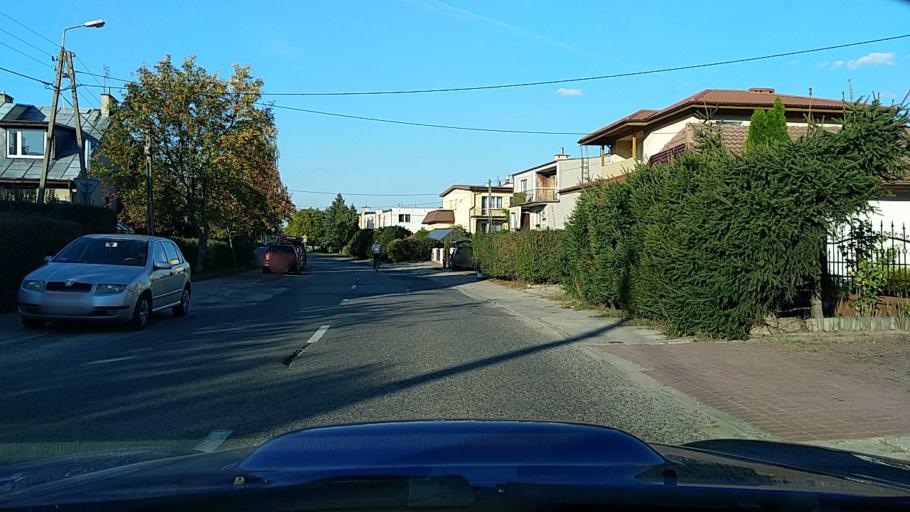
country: PL
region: Warmian-Masurian Voivodeship
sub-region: Olsztyn
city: Kortowo
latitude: 53.7665
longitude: 20.4181
